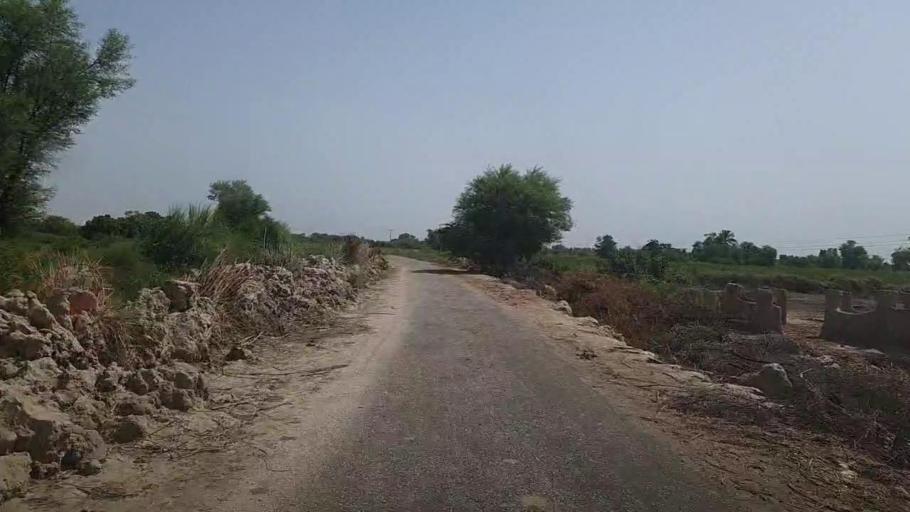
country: PK
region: Sindh
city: Pad Idan
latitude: 26.8247
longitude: 68.3281
